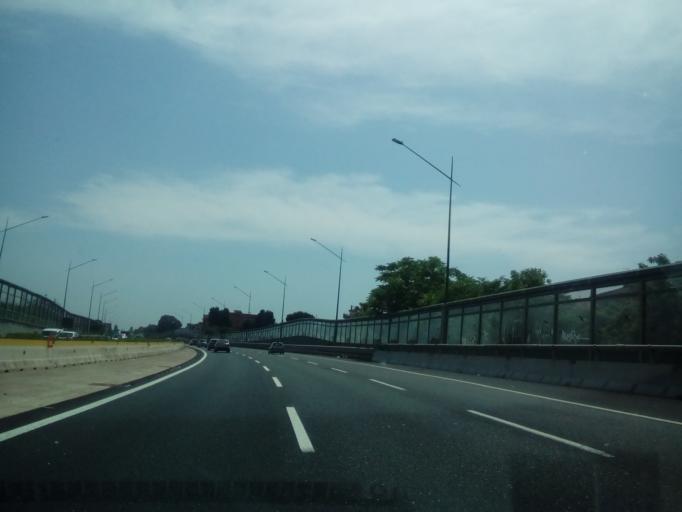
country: IT
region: Latium
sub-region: Citta metropolitana di Roma Capitale
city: Valle Santa
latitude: 41.9551
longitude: 12.3836
